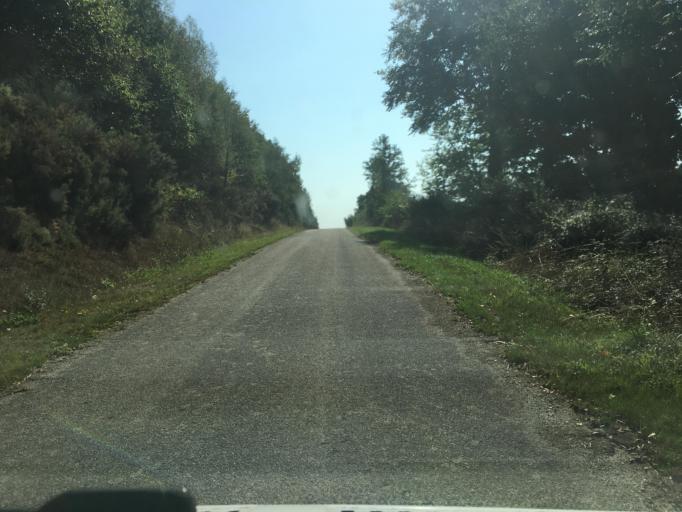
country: FR
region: Brittany
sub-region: Departement des Cotes-d'Armor
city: Mur-de-Bretagne
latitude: 48.2204
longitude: -3.0236
